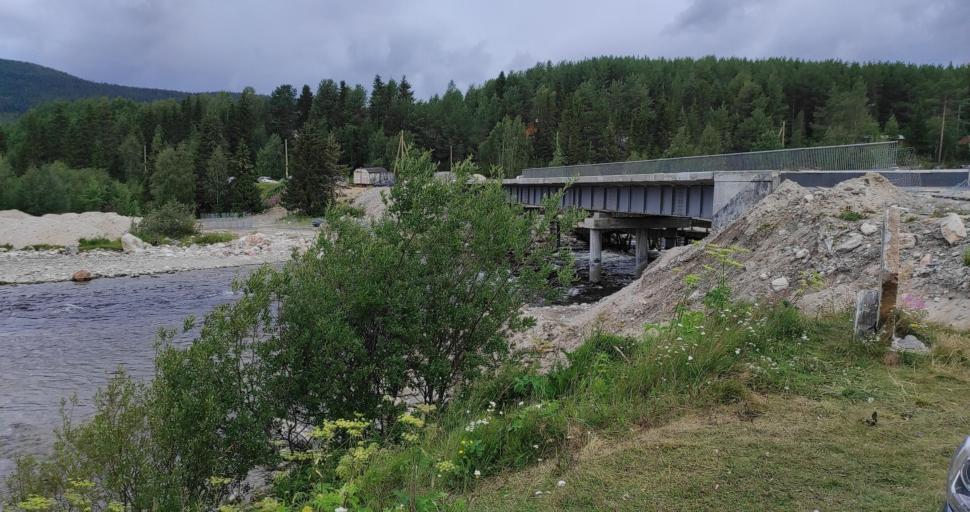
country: RU
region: Murmansk
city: Afrikanda
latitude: 67.0832
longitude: 32.9964
